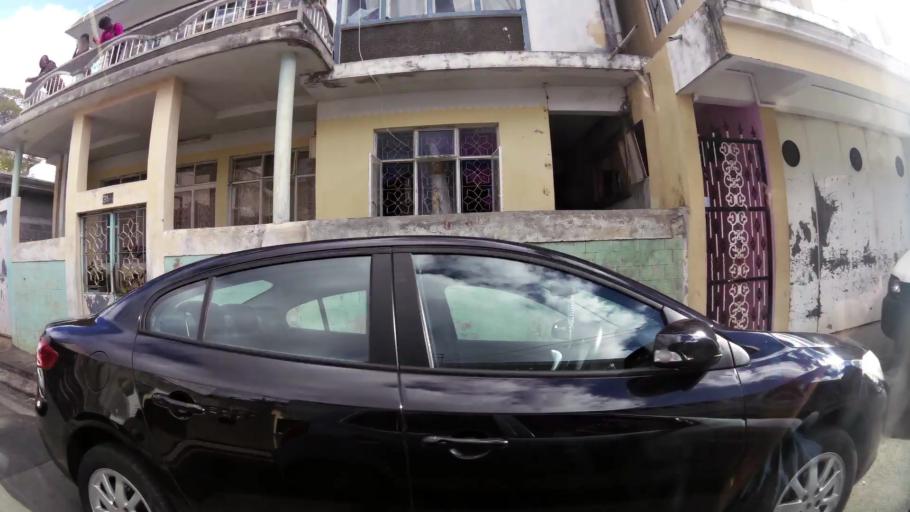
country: MU
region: Pamplemousses
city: Le Hochet
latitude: -20.1538
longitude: 57.5170
